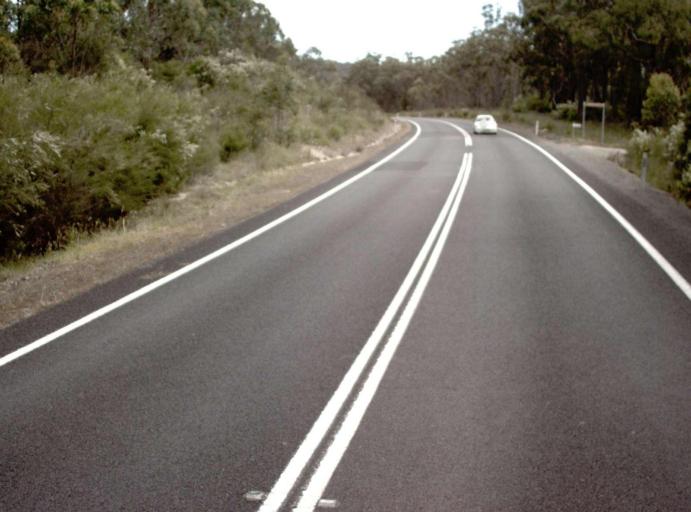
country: AU
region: New South Wales
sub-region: Bega Valley
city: Eden
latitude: -37.4834
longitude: 149.5517
